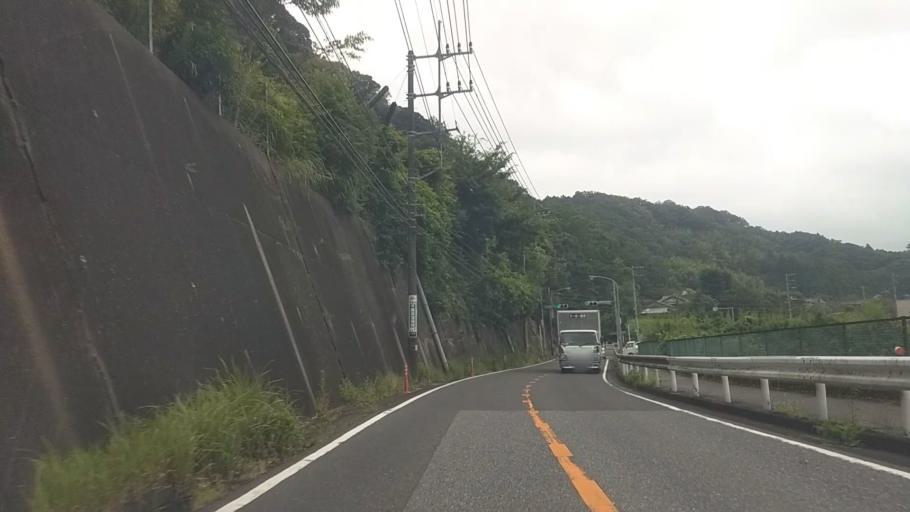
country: JP
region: Chiba
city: Kisarazu
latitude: 35.2921
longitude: 140.0824
